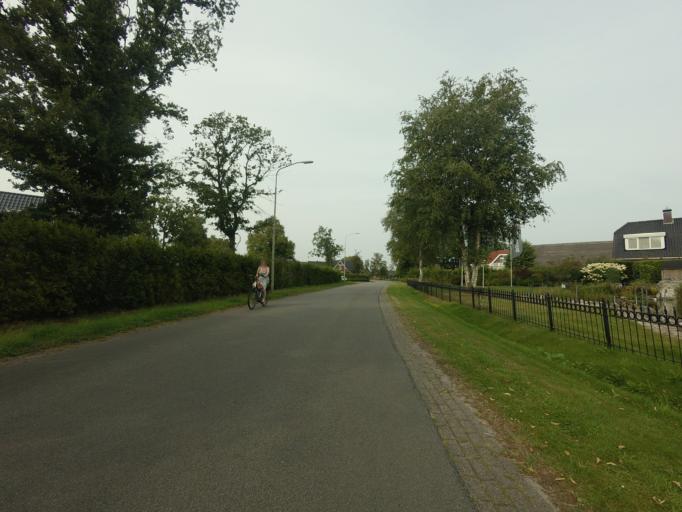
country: NL
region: Drenthe
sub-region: Gemeente Tynaarlo
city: Vries
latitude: 53.1282
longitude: 6.5664
